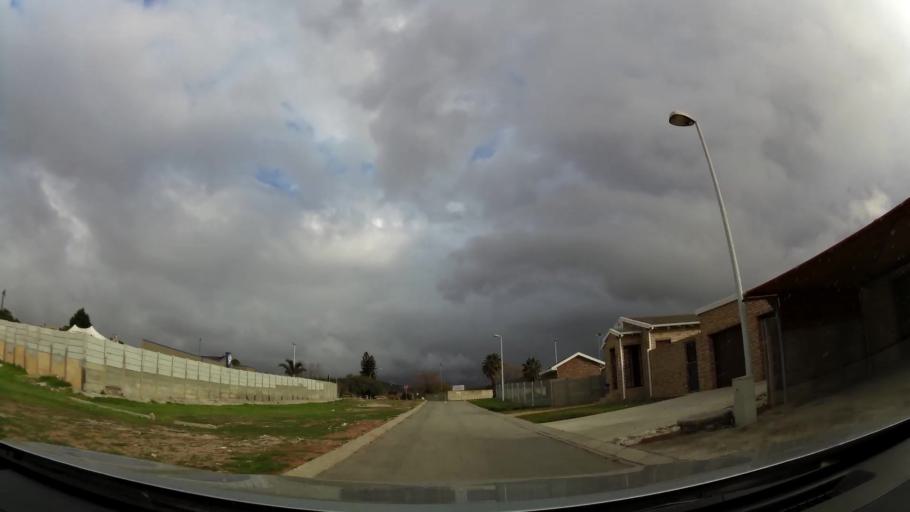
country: ZA
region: Eastern Cape
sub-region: Nelson Mandela Bay Metropolitan Municipality
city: Uitenhage
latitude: -33.7996
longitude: 25.4554
